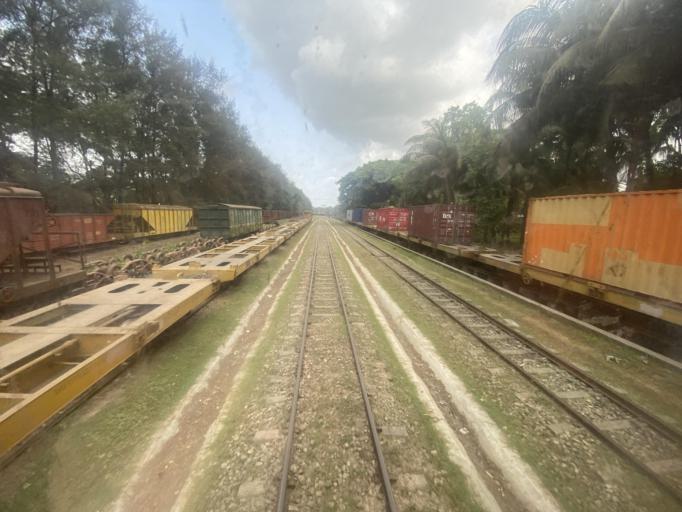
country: BD
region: Chittagong
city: Chittagong
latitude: 22.3232
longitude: 91.7807
